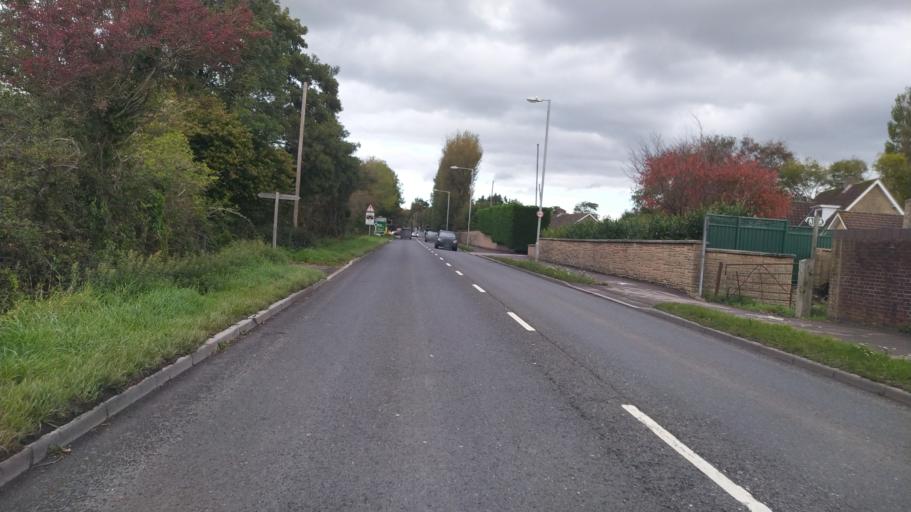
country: GB
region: England
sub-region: Dorset
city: Bridport
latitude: 50.7303
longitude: -2.7519
